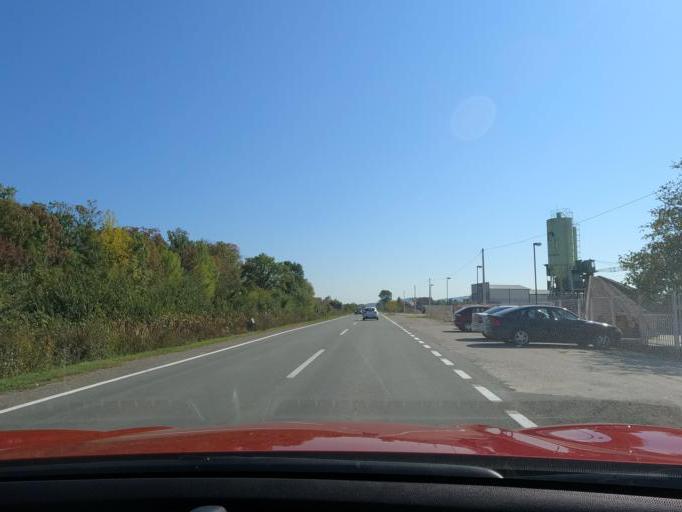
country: RS
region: Central Serbia
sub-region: Raski Okrug
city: Vrnjacka Banja
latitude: 43.6456
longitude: 20.9015
